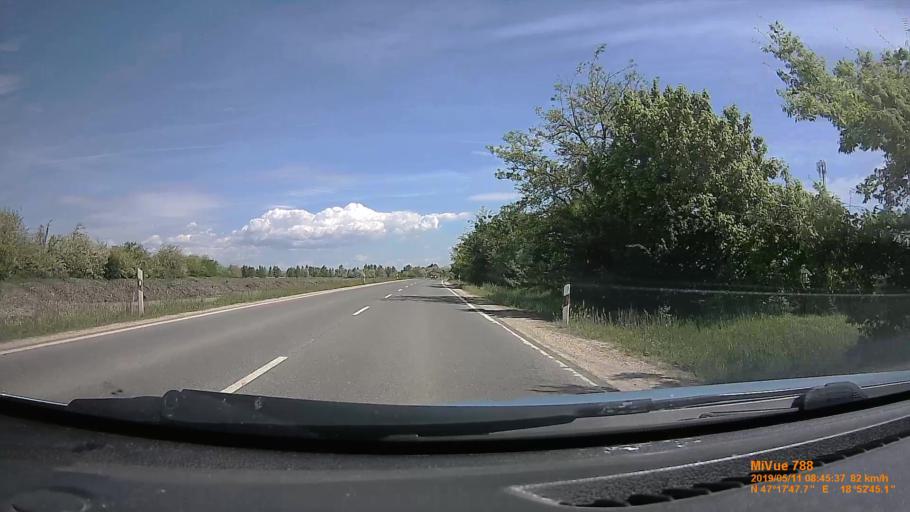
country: HU
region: Fejer
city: Ercsi
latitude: 47.2967
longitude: 18.8794
